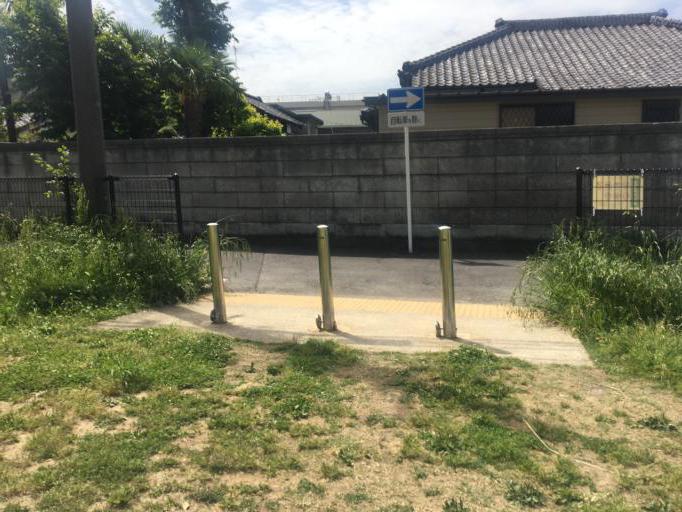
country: JP
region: Saitama
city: Yono
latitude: 35.8589
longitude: 139.6266
